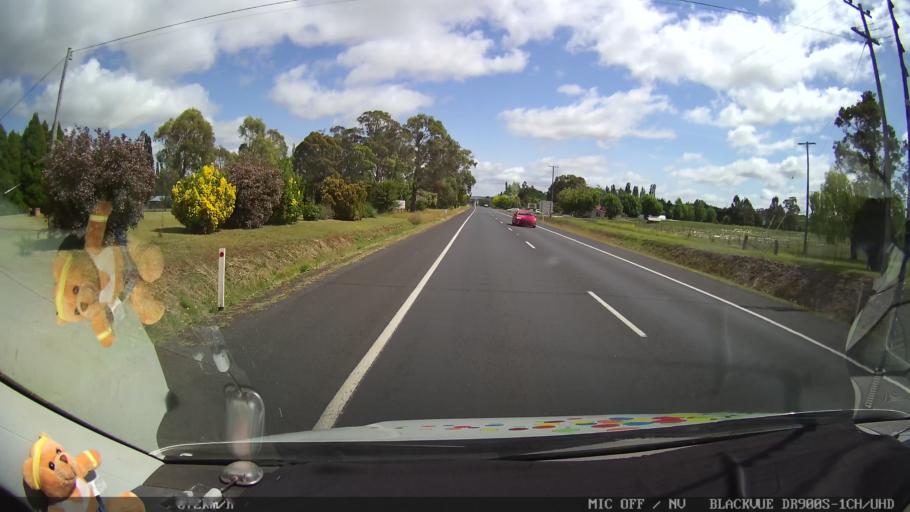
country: AU
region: New South Wales
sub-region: Glen Innes Severn
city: Glen Innes
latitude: -29.7631
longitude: 151.7335
